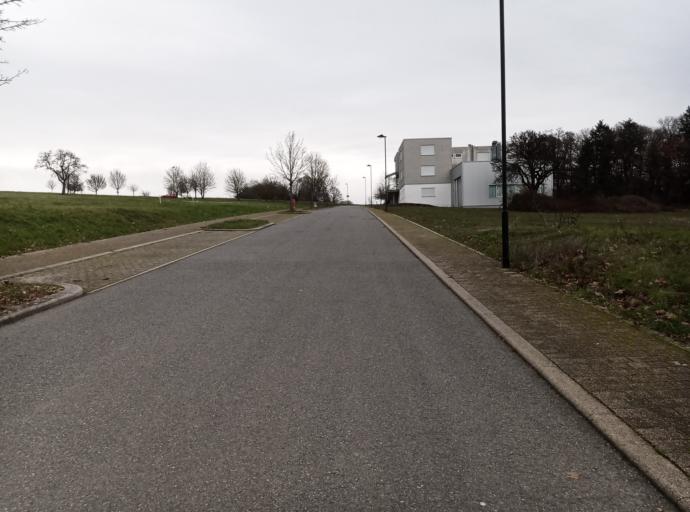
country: DE
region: Baden-Wuerttemberg
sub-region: Karlsruhe Region
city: Binau
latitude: 49.3493
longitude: 9.0441
